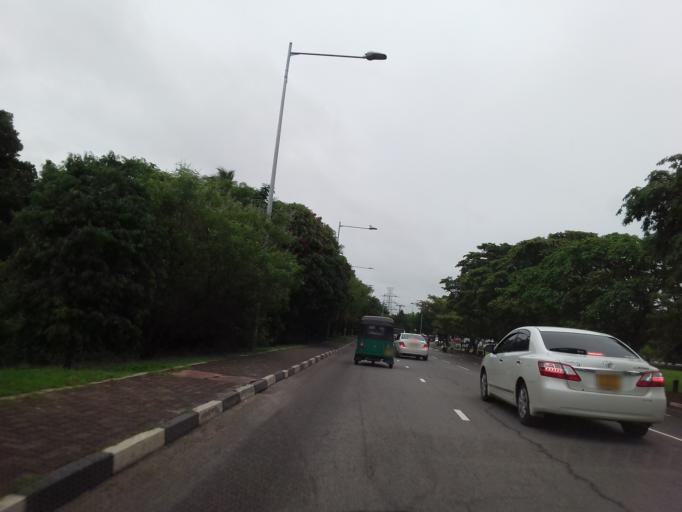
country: LK
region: Western
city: Battaramulla South
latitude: 6.8934
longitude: 79.9203
